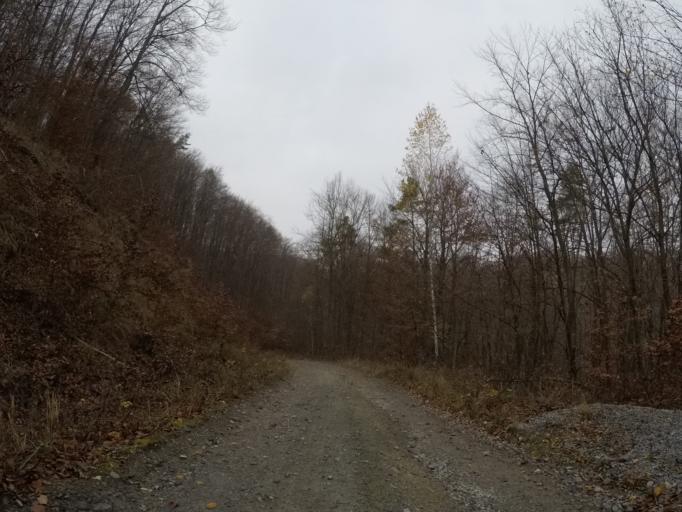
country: SK
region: Presovsky
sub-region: Okres Presov
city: Presov
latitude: 48.8902
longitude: 21.1996
